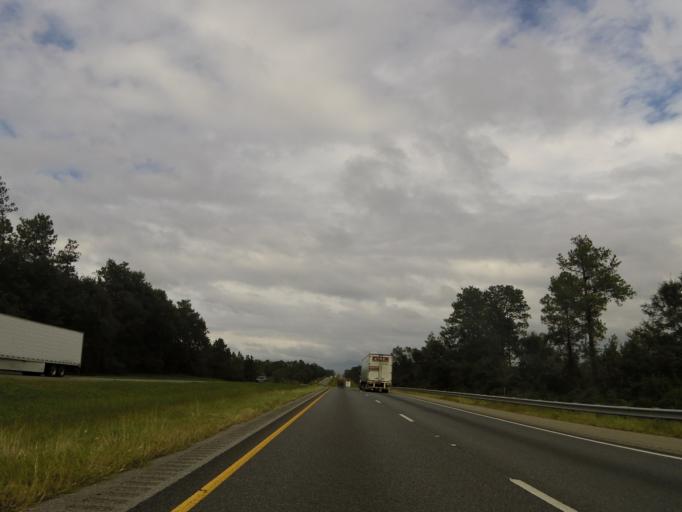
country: US
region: Alabama
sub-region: Escambia County
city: Brewton
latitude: 31.2567
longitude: -87.2306
